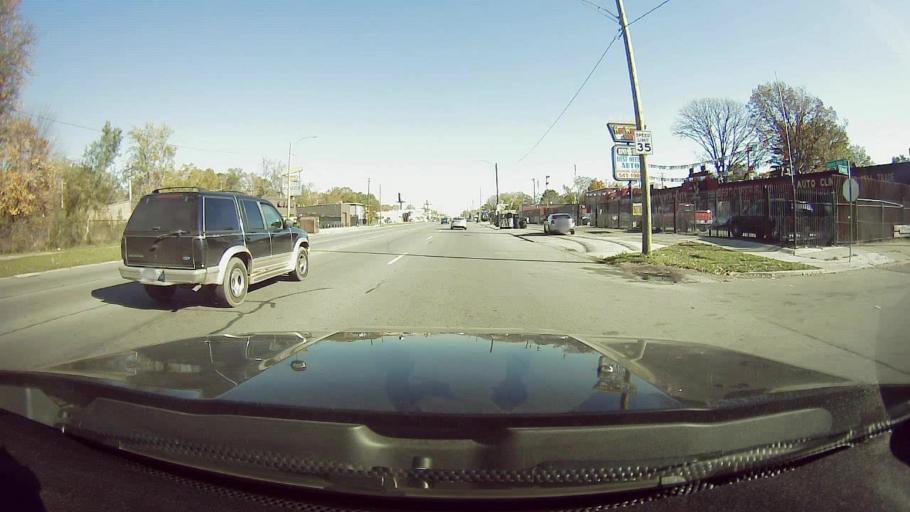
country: US
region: Michigan
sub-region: Oakland County
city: Southfield
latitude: 42.4299
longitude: -83.2242
